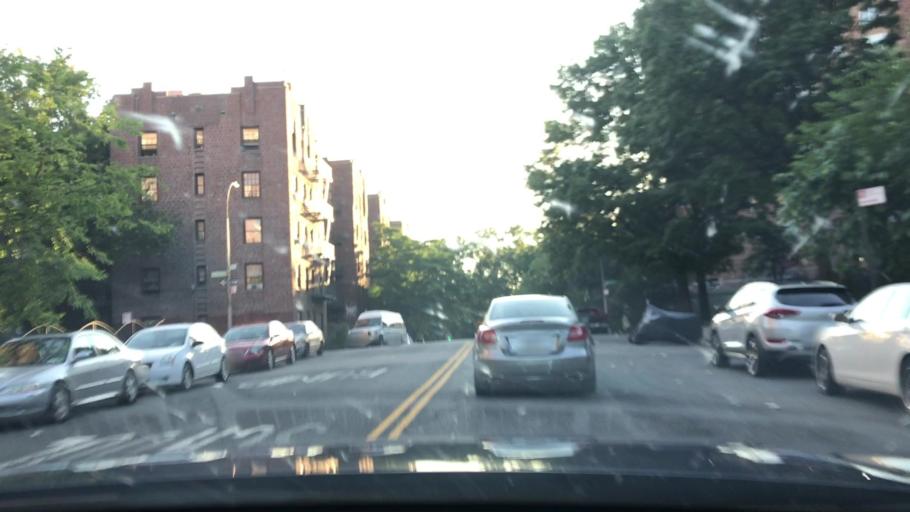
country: US
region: New York
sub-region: Bronx
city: The Bronx
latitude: 40.8679
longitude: -73.8687
